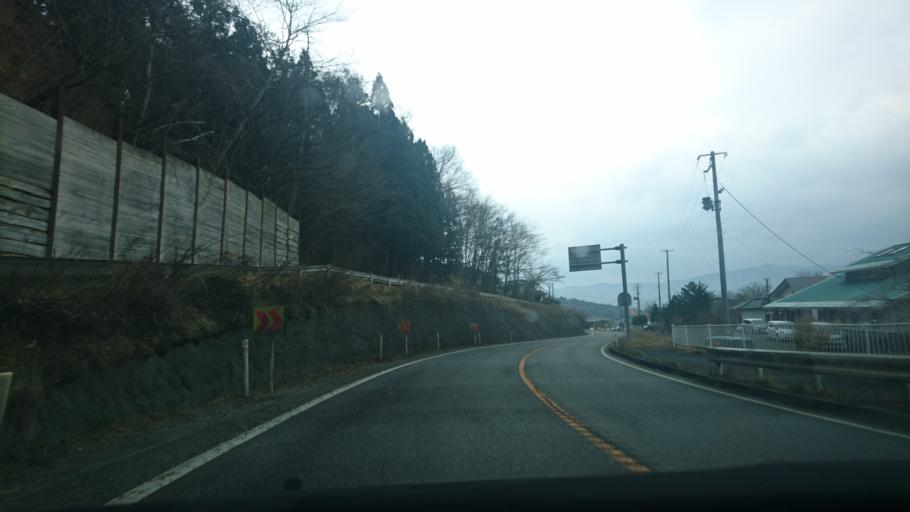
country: JP
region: Iwate
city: Ofunato
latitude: 39.0212
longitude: 141.6741
